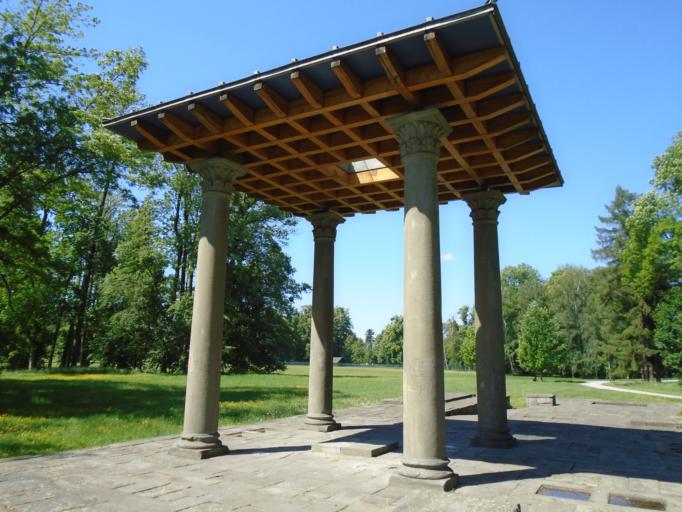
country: PL
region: Silesian Voivodeship
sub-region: Powiat cieszynski
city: Kaczyce
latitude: 49.8427
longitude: 18.6003
